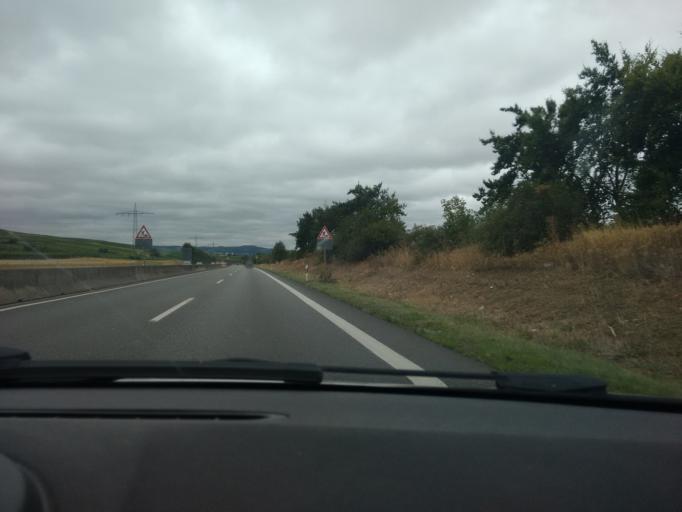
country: DE
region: Rheinland-Pfalz
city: Biebelsheim
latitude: 49.8816
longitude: 7.9319
